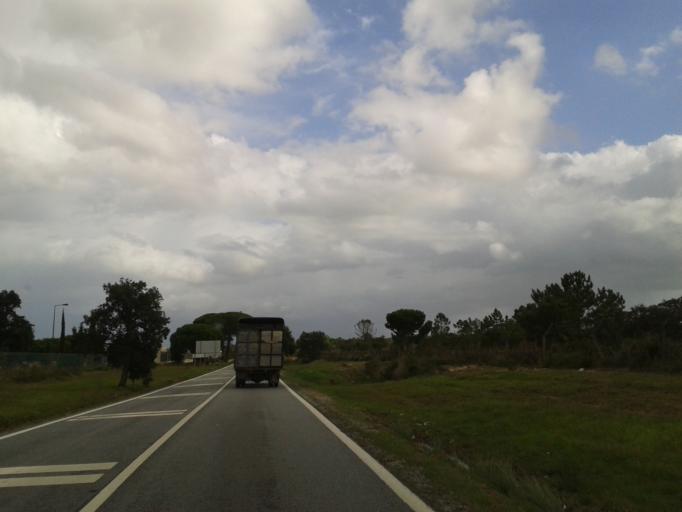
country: PT
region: Setubal
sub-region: Alcochete
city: Alcochete
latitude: 38.7833
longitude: -8.8791
